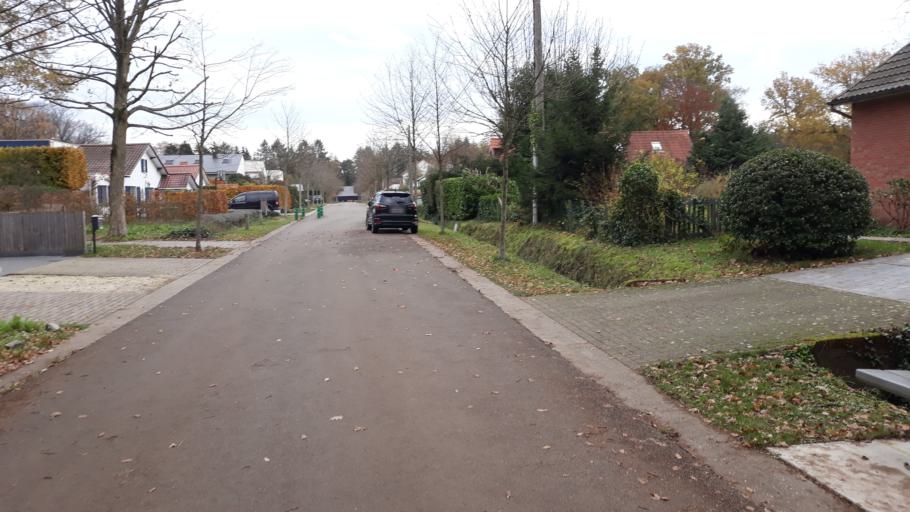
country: BE
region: Flanders
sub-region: Provincie Antwerpen
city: Vorselaar
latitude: 51.1732
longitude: 4.7784
